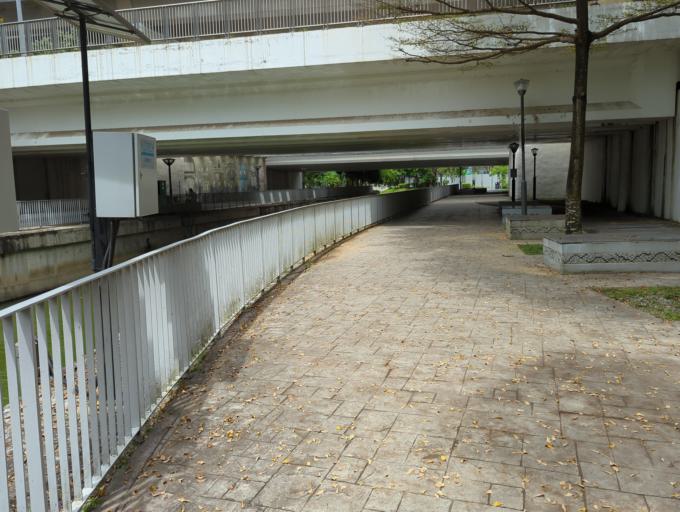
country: MY
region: Johor
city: Kampung Pasir Gudang Baru
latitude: 1.4091
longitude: 103.8994
